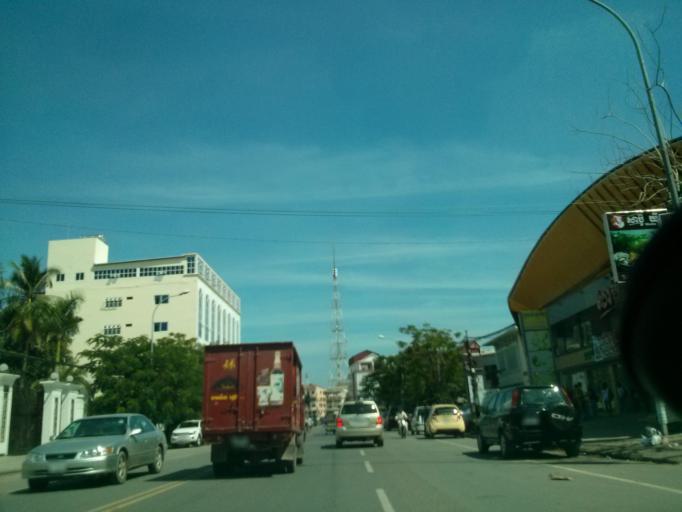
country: KH
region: Phnom Penh
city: Phnom Penh
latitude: 11.5829
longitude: 104.8981
